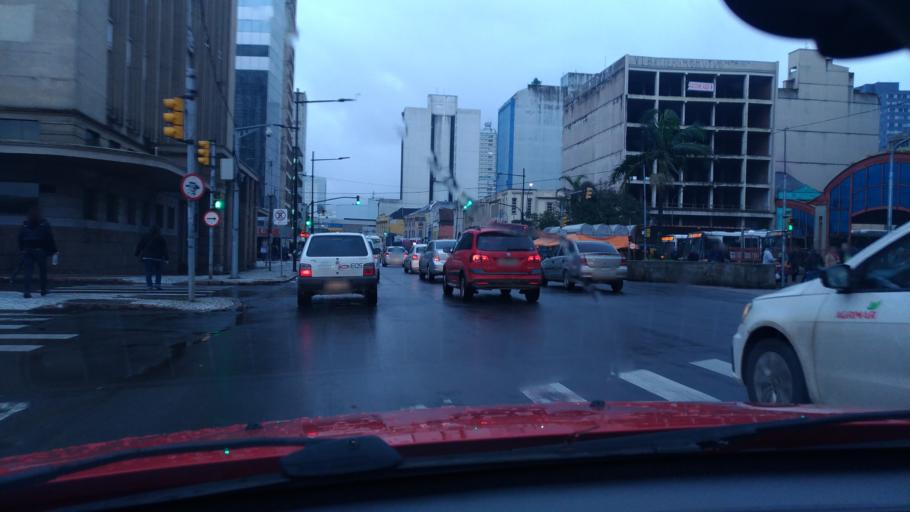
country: BR
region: Rio Grande do Sul
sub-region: Porto Alegre
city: Porto Alegre
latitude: -30.0268
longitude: -51.2277
